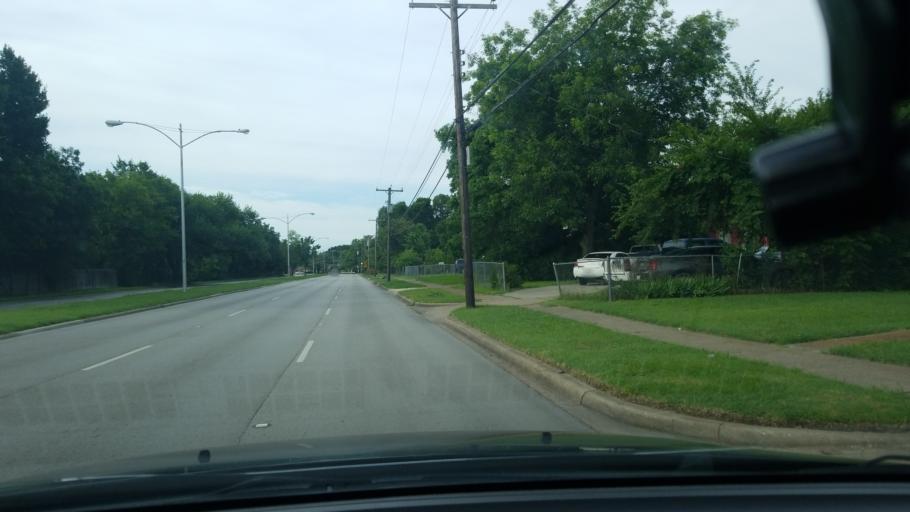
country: US
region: Texas
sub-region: Dallas County
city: Balch Springs
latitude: 32.7580
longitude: -96.6656
